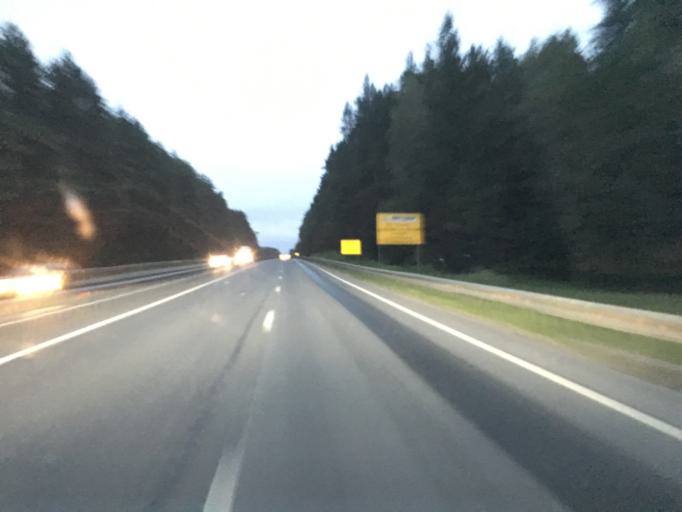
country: RU
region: Kaluga
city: Maloyaroslavets
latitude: 54.9610
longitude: 36.4636
